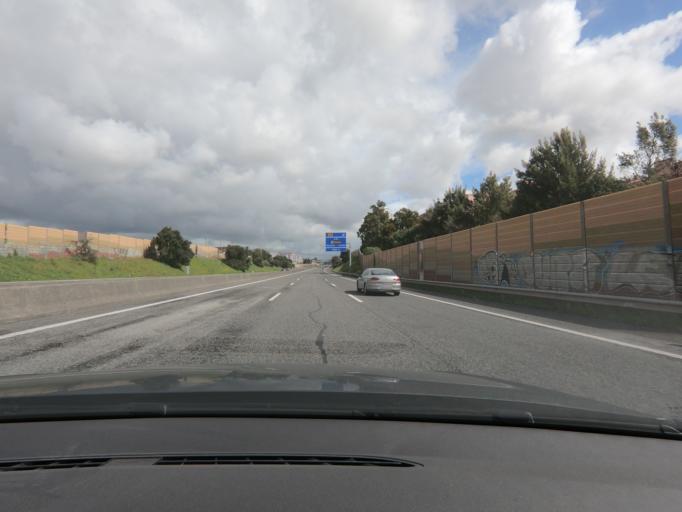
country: PT
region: Lisbon
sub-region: Sintra
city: Queluz
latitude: 38.7512
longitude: -9.2725
